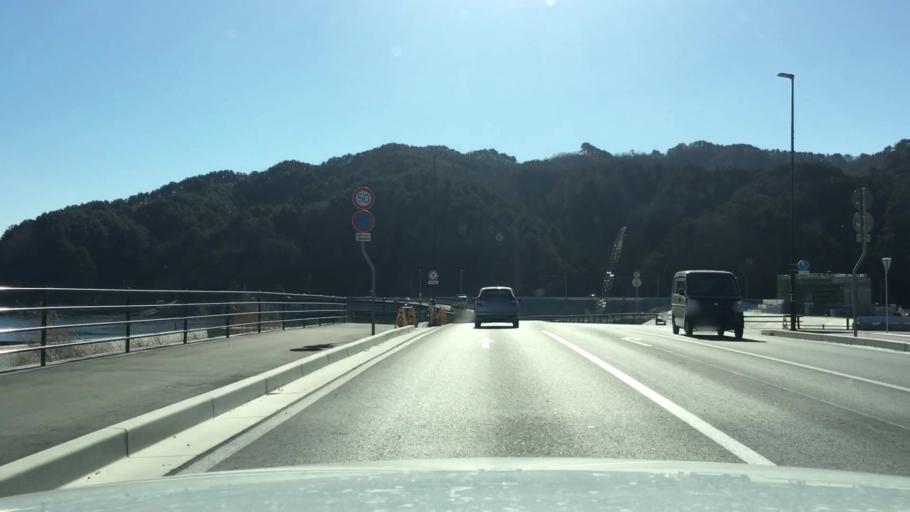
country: JP
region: Iwate
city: Yamada
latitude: 39.4515
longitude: 141.9617
